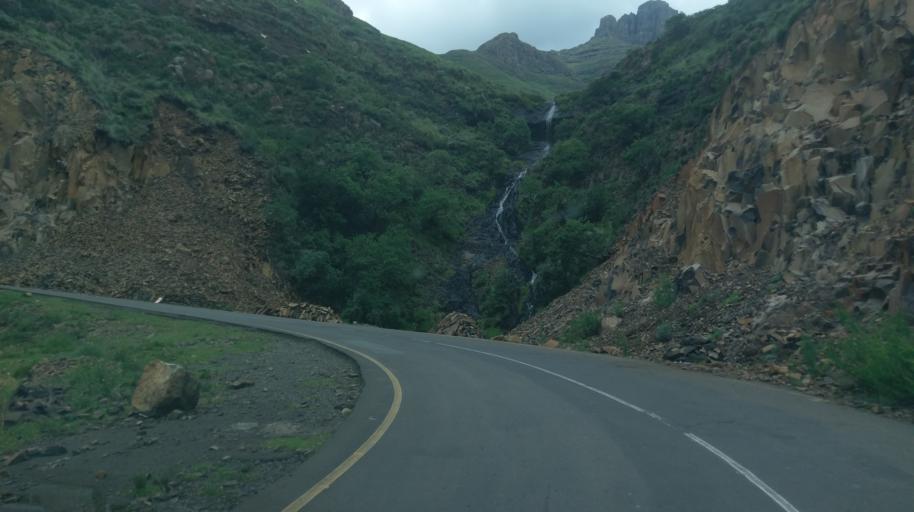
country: LS
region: Butha-Buthe
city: Butha-Buthe
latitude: -29.0546
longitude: 28.3453
